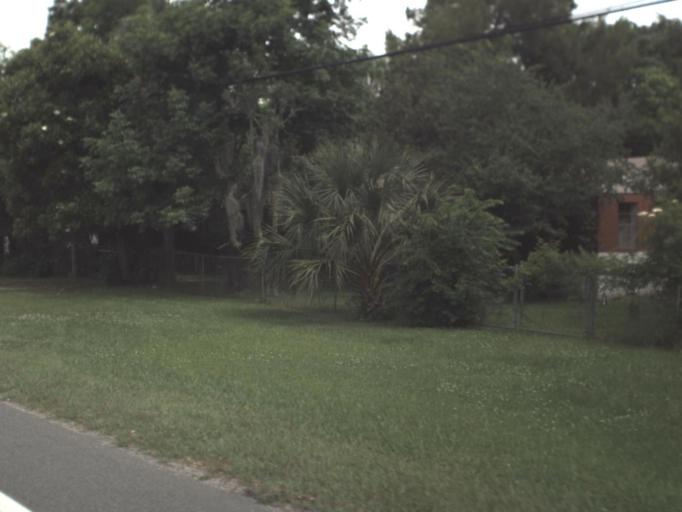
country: US
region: Florida
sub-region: Duval County
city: Atlantic Beach
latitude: 30.4117
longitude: -81.5189
